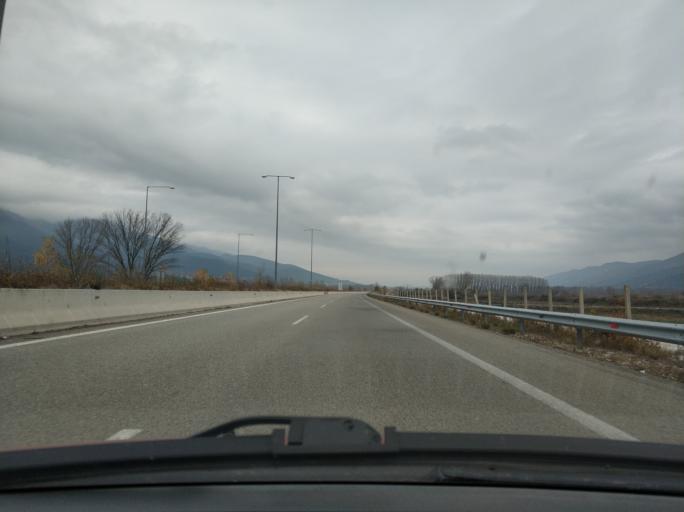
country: GR
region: East Macedonia and Thrace
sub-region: Nomos Kavalas
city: Nikisiani
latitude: 40.8424
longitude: 24.1199
